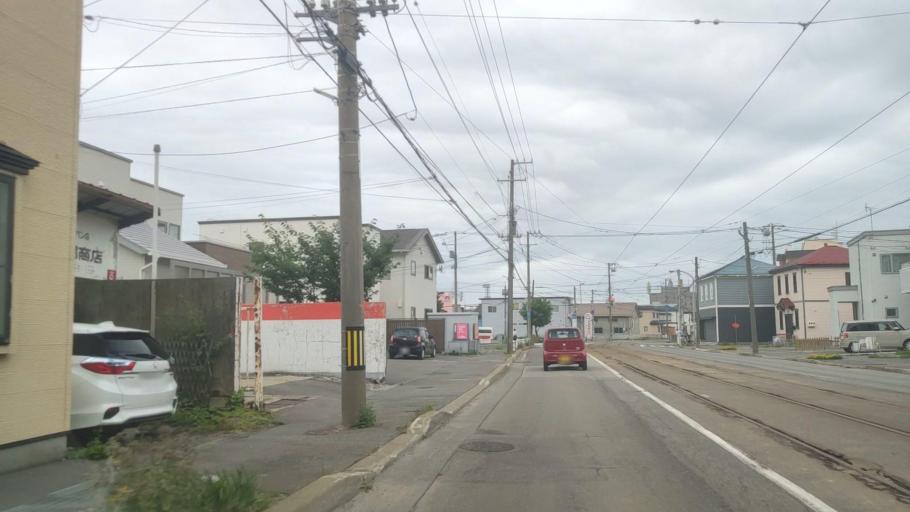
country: JP
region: Hokkaido
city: Hakodate
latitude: 41.7705
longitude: 140.7087
